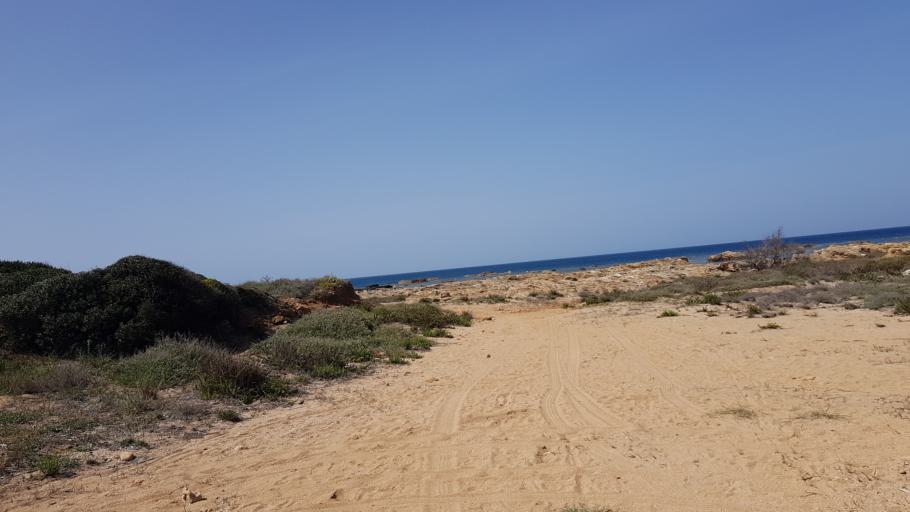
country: IT
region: Apulia
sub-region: Provincia di Brindisi
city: Materdomini
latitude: 40.6840
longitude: 17.9351
